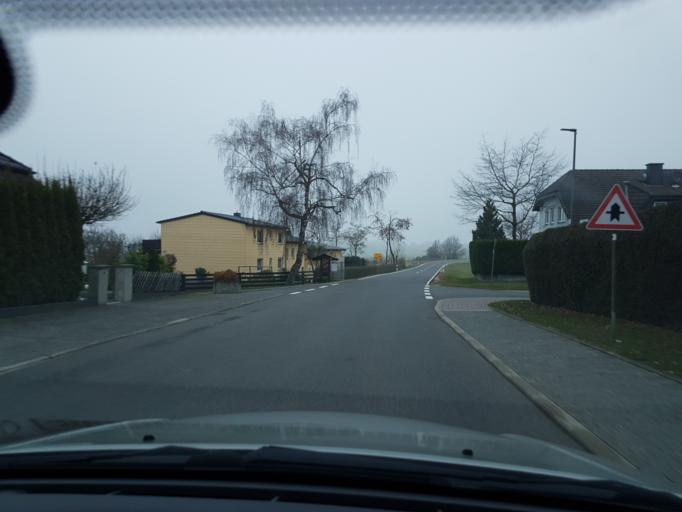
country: DE
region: Hesse
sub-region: Regierungsbezirk Darmstadt
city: Schlangenbad
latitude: 50.0850
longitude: 8.0434
